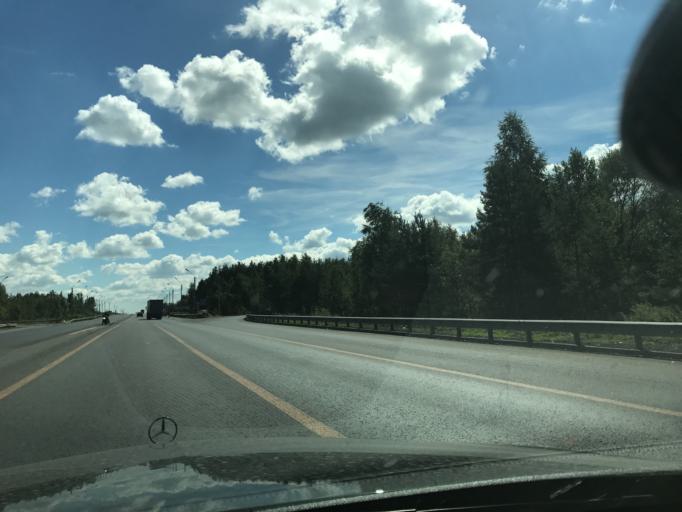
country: RU
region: Nizjnij Novgorod
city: Gorbatovka
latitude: 56.2676
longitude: 43.7049
